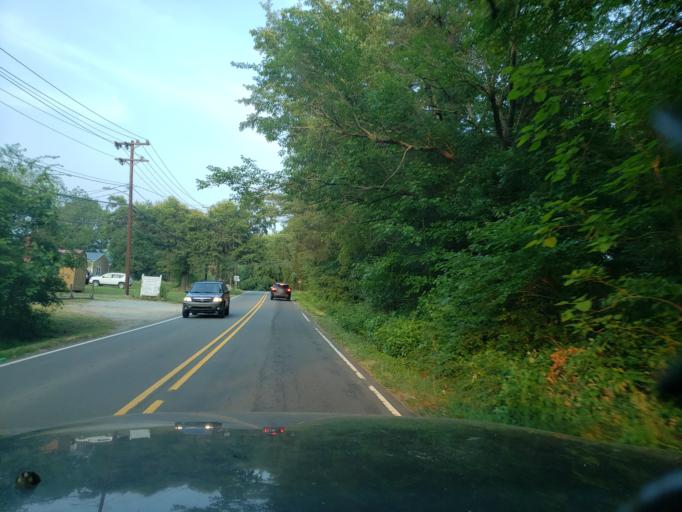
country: US
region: North Carolina
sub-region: Durham County
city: Durham
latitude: 35.9579
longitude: -78.8741
